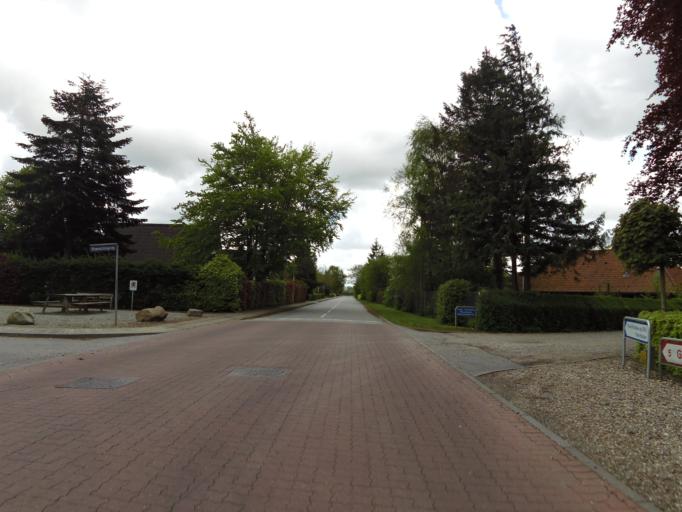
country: DK
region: South Denmark
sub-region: Haderslev Kommune
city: Gram
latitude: 55.3153
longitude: 8.9831
